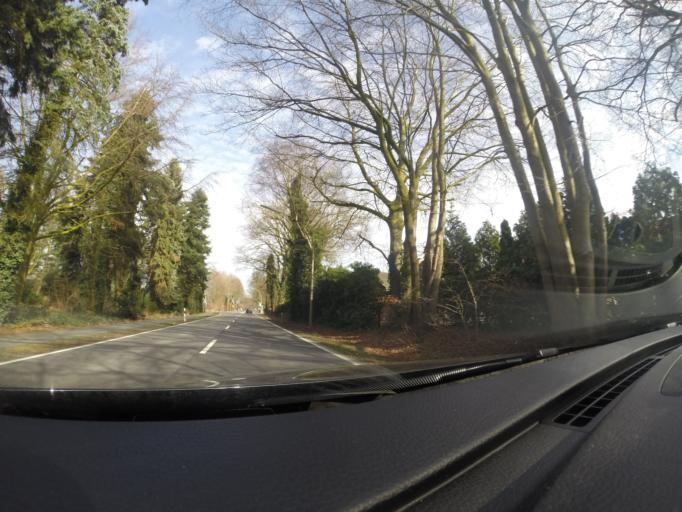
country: DE
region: North Rhine-Westphalia
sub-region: Regierungsbezirk Munster
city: Vreden
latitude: 52.0405
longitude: 6.8455
